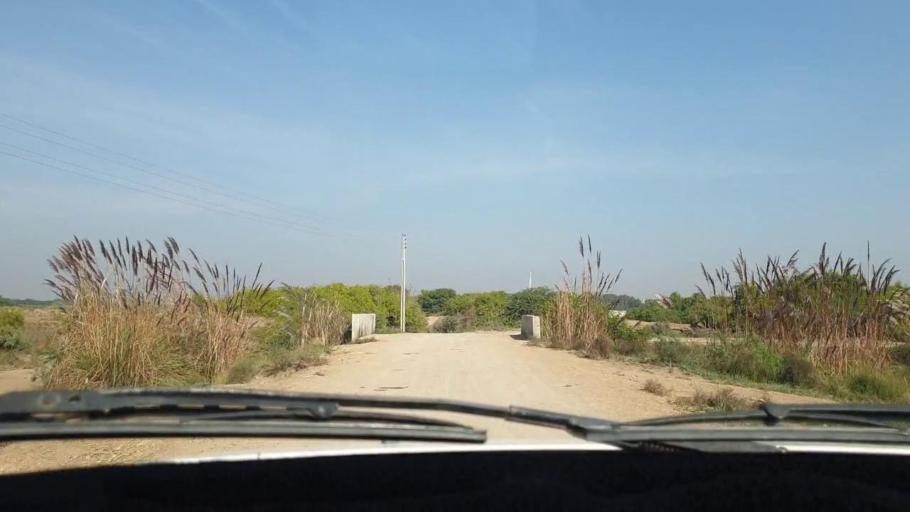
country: PK
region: Sindh
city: Tando Muhammad Khan
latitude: 24.9929
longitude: 68.4651
